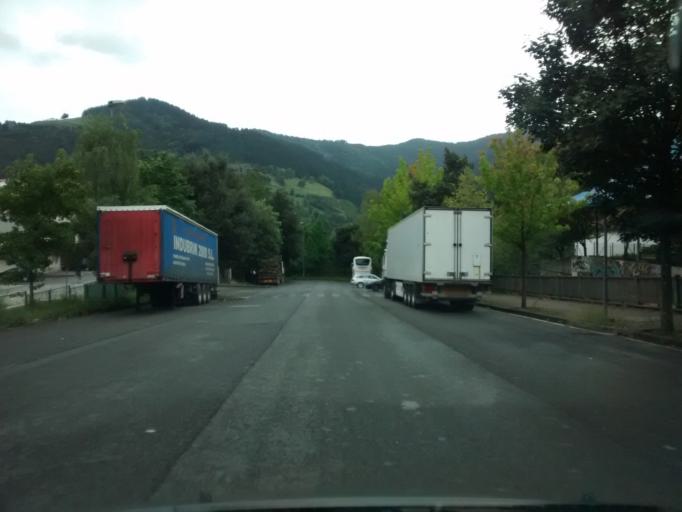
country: ES
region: Basque Country
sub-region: Provincia de Guipuzcoa
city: Eibar
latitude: 43.1959
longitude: -2.4545
